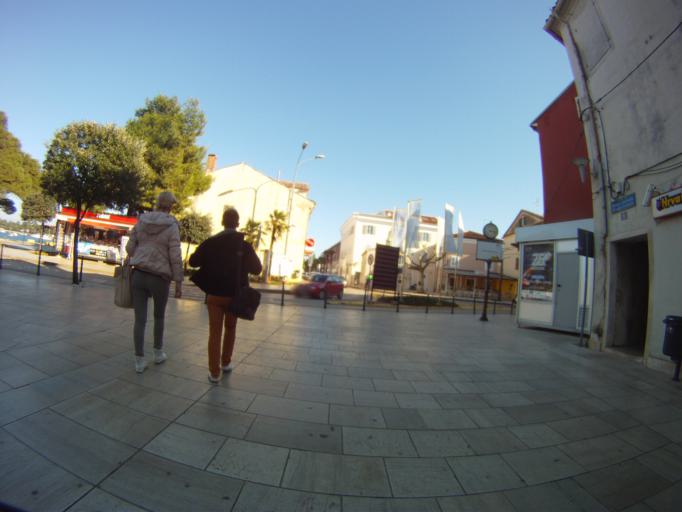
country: HR
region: Istarska
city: Umag
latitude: 45.4332
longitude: 13.5199
